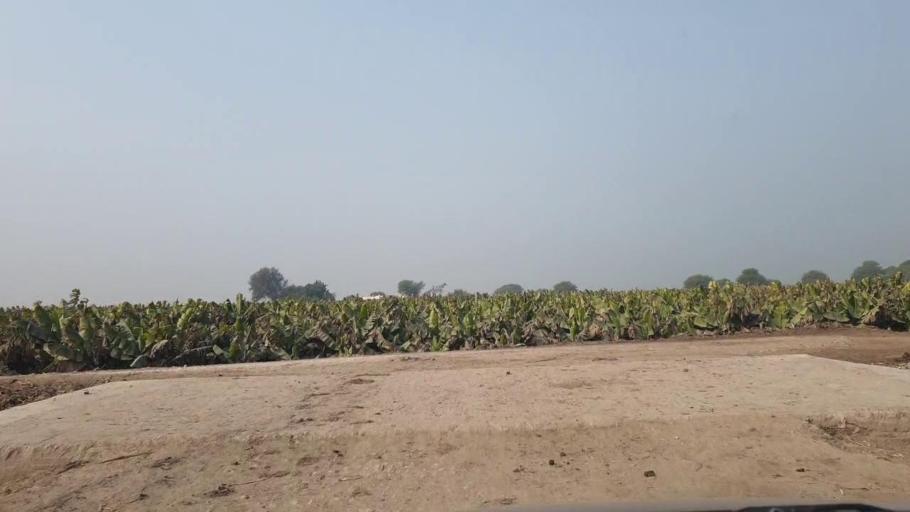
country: PK
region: Sindh
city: Hala
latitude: 25.8820
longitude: 68.3556
